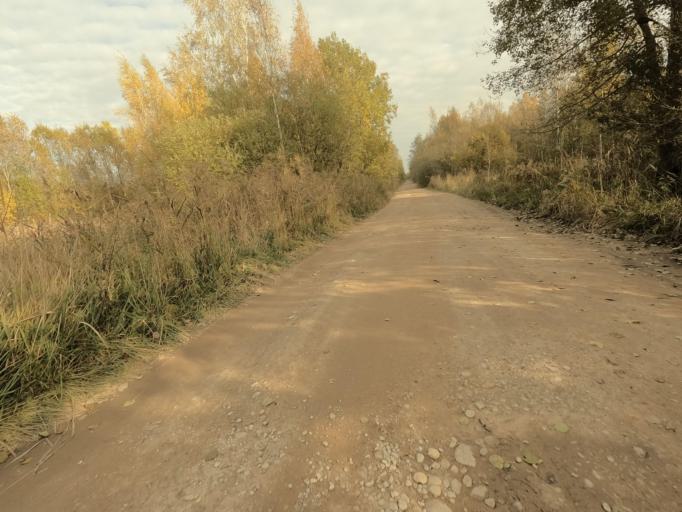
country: RU
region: Novgorod
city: Pankovka
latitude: 58.8958
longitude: 31.0074
